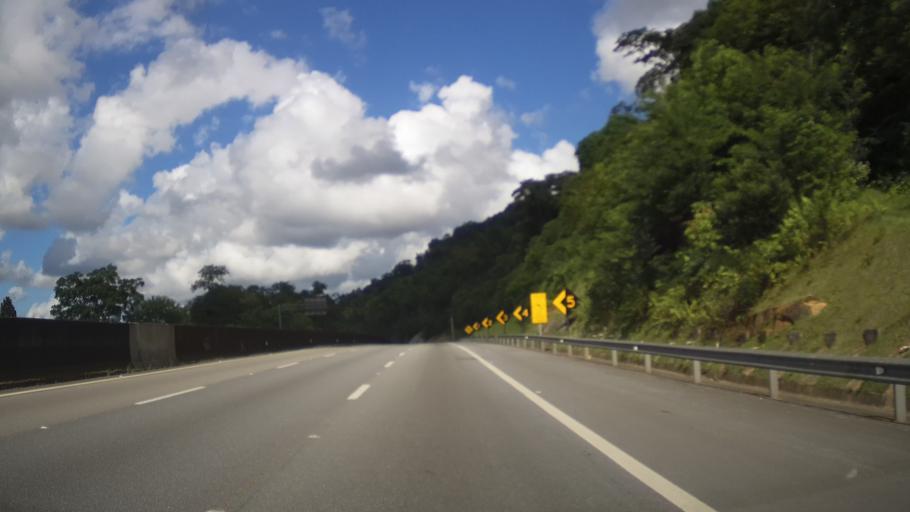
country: BR
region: Sao Paulo
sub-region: Cubatao
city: Cubatao
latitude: -23.9300
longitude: -46.4617
